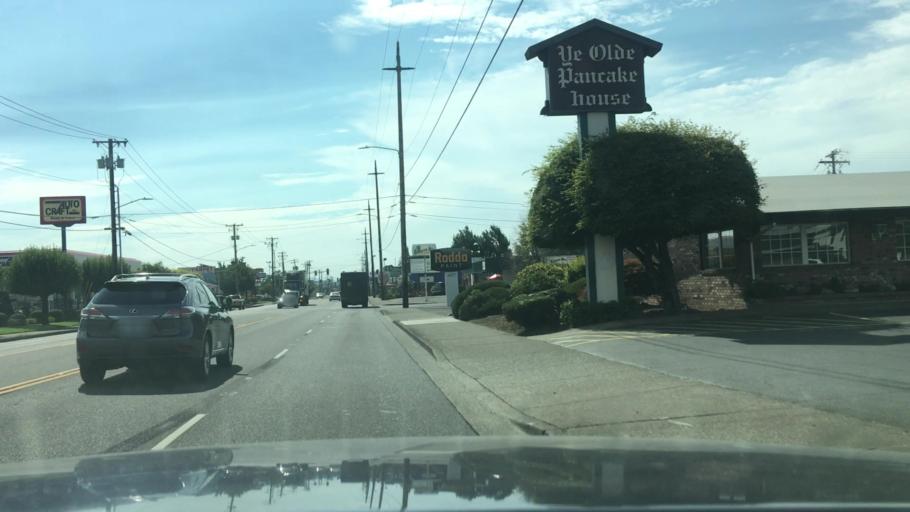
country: US
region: Oregon
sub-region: Lane County
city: Eugene
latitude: 44.0479
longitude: -123.1309
